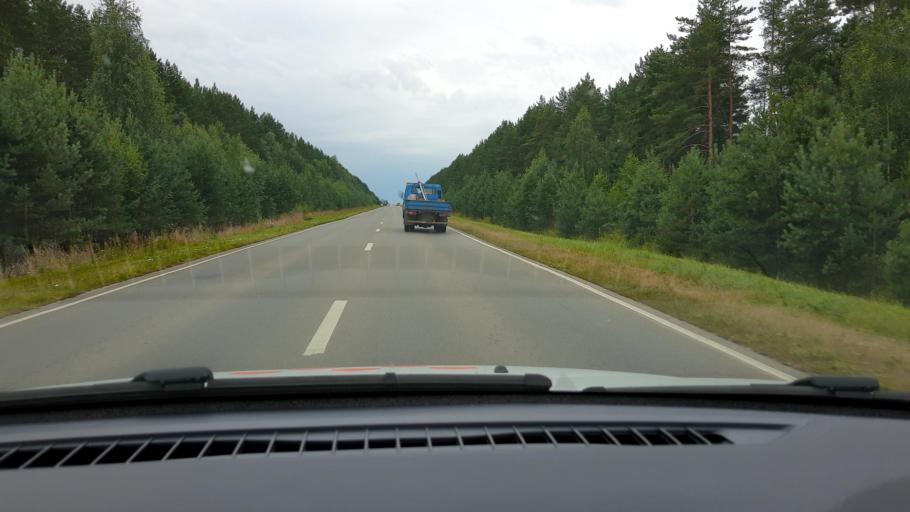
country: RU
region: Nizjnij Novgorod
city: Vyyezdnoye
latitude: 55.1603
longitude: 43.5818
